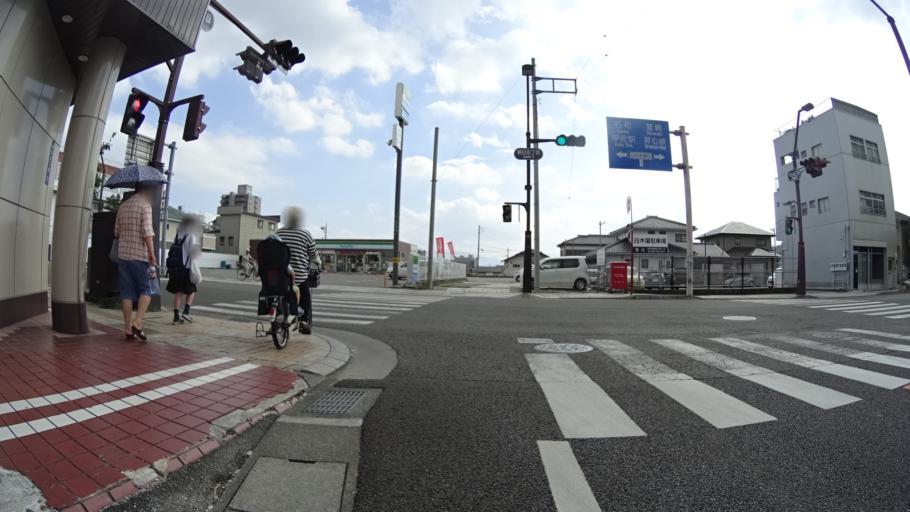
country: JP
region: Yamanashi
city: Kofu-shi
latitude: 35.6737
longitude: 138.5666
